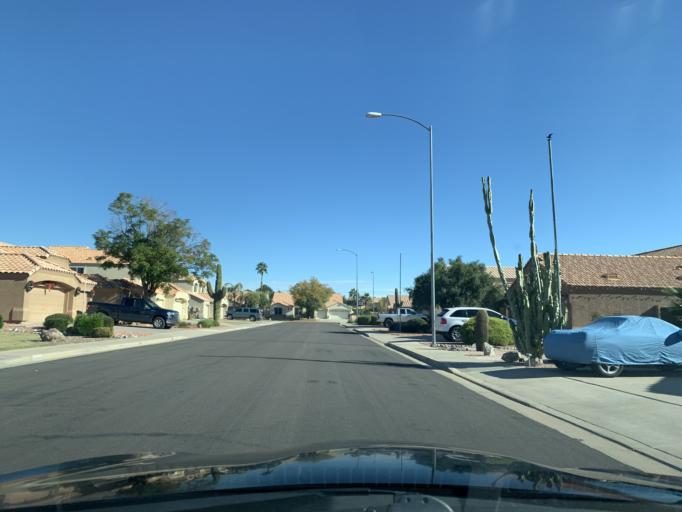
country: US
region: Arizona
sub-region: Pinal County
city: Apache Junction
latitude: 33.3842
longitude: -111.6231
